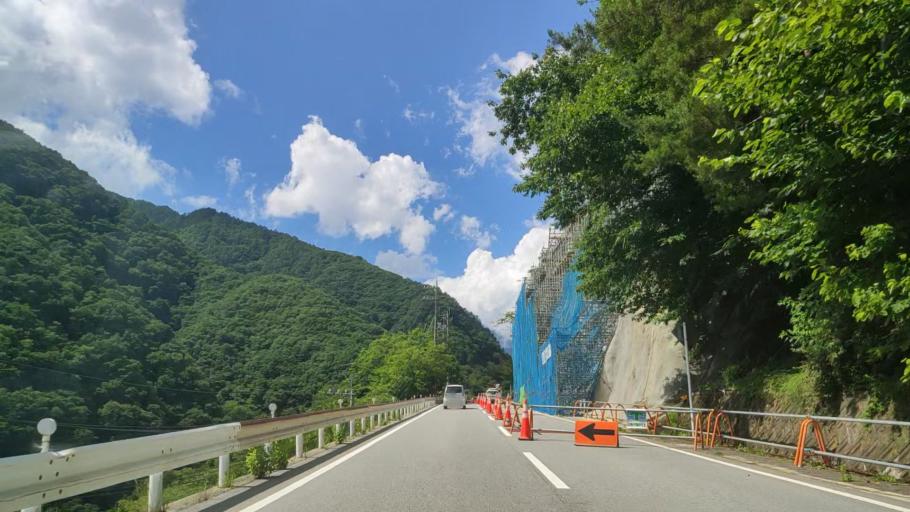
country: JP
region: Yamanashi
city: Enzan
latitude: 35.8307
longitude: 138.7645
